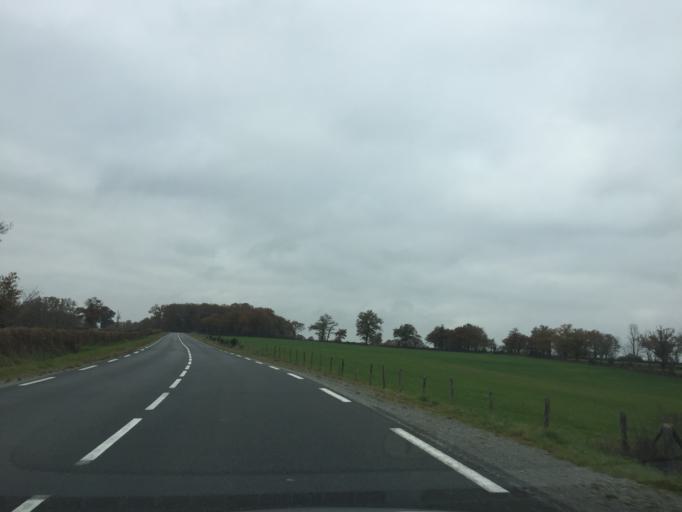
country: FR
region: Limousin
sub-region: Departement de la Creuse
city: Gouzon
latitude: 46.1787
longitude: 2.2263
